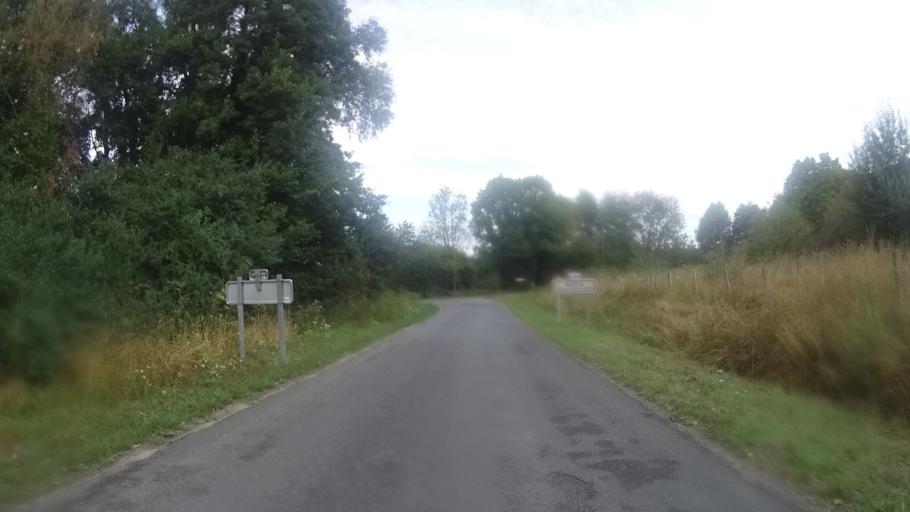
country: FR
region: Centre
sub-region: Departement du Loiret
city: Fay-aux-Loges
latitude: 47.9372
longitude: 2.1903
